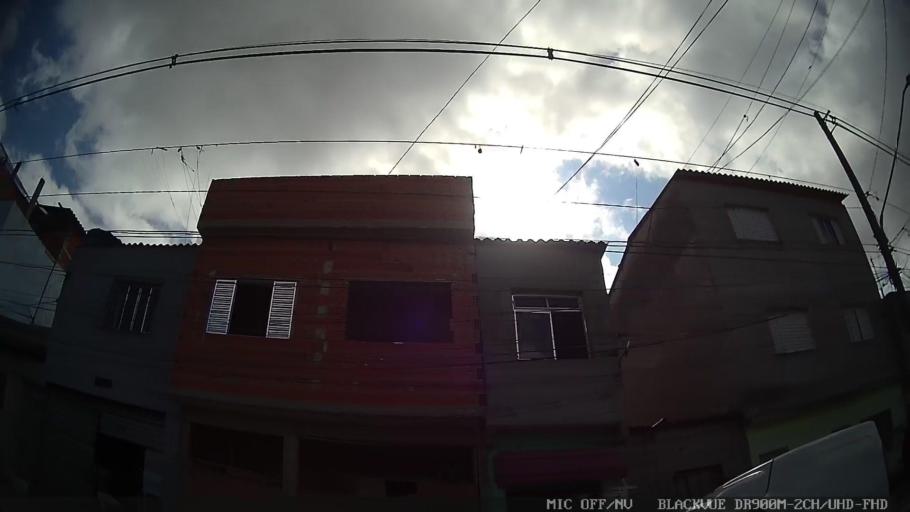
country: BR
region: Sao Paulo
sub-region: Guarulhos
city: Guarulhos
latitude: -23.5187
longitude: -46.4761
